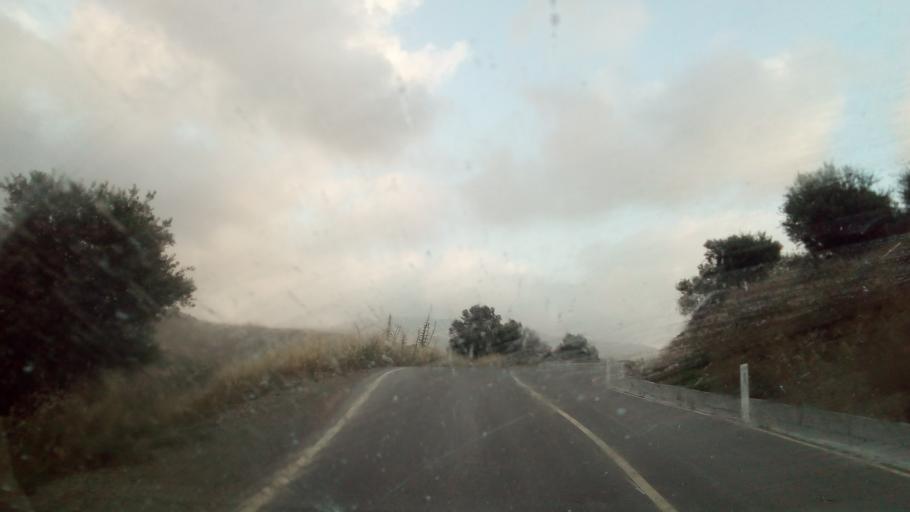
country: CY
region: Limassol
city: Pachna
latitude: 34.8517
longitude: 32.6517
